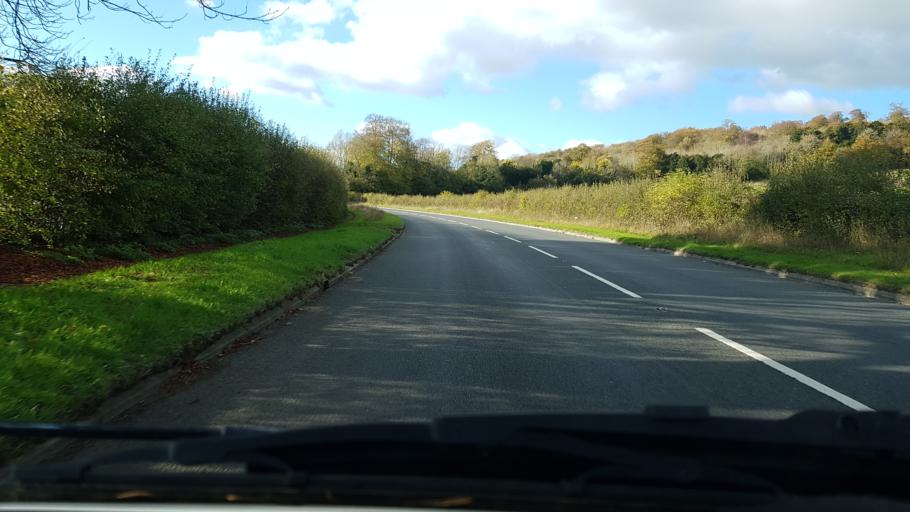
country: GB
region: England
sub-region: Surrey
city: East Horsley
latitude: 51.2223
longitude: -0.4621
